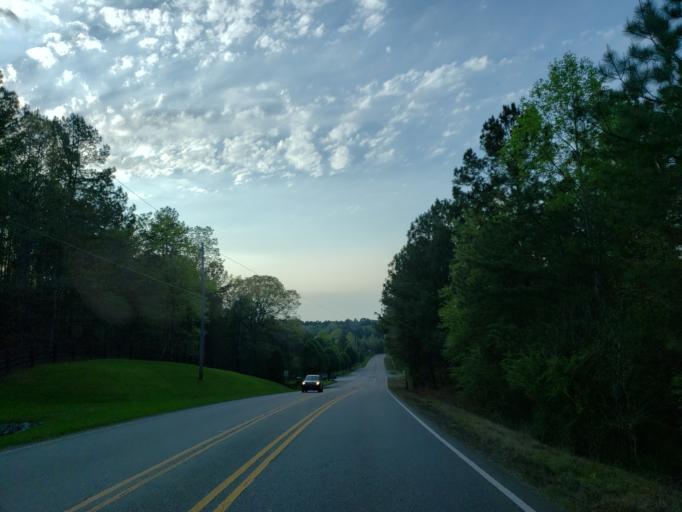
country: US
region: Georgia
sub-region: Cherokee County
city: Ball Ground
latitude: 34.2857
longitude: -84.3823
